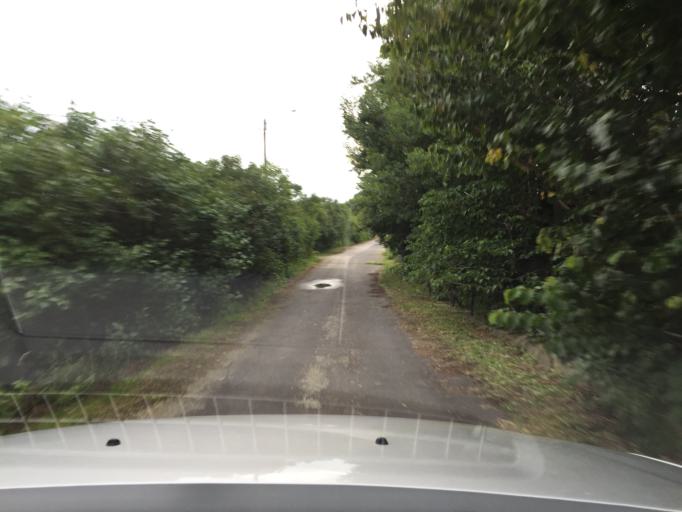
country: SE
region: Skane
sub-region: Kristianstads Kommun
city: Norra Asum
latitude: 55.9382
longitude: 14.0738
